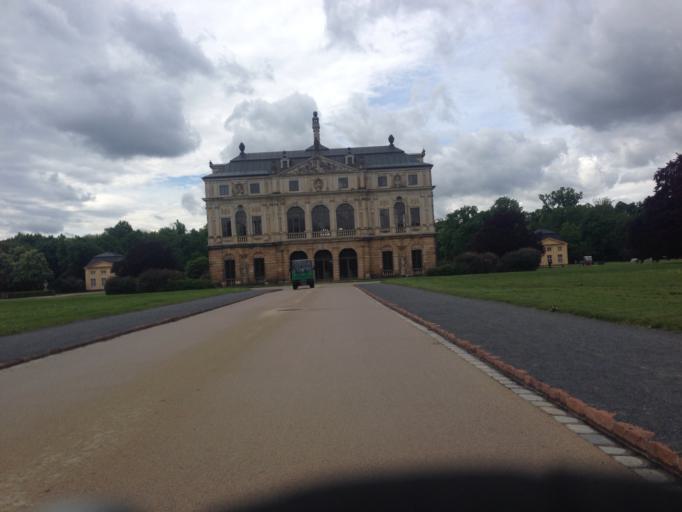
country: DE
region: Saxony
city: Dresden
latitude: 51.0387
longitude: 13.7637
